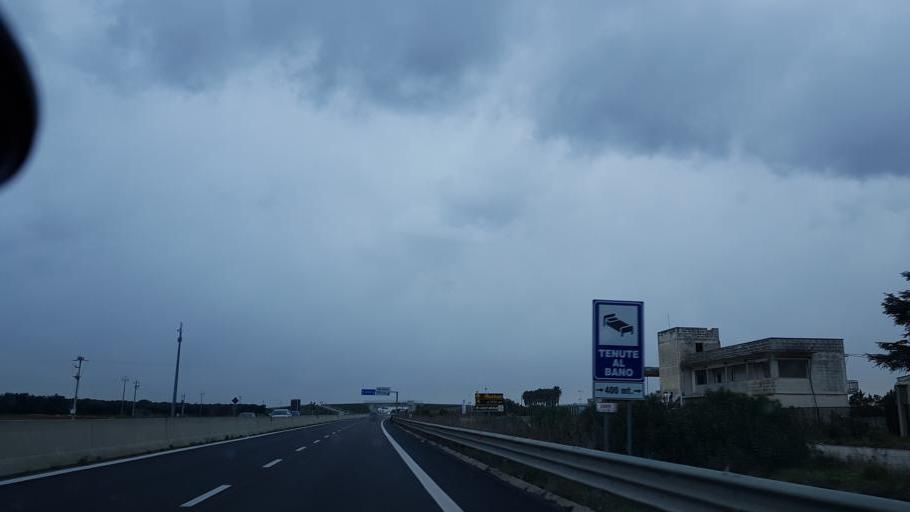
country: IT
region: Apulia
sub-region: Provincia di Brindisi
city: Mesagne
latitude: 40.5942
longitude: 17.8654
